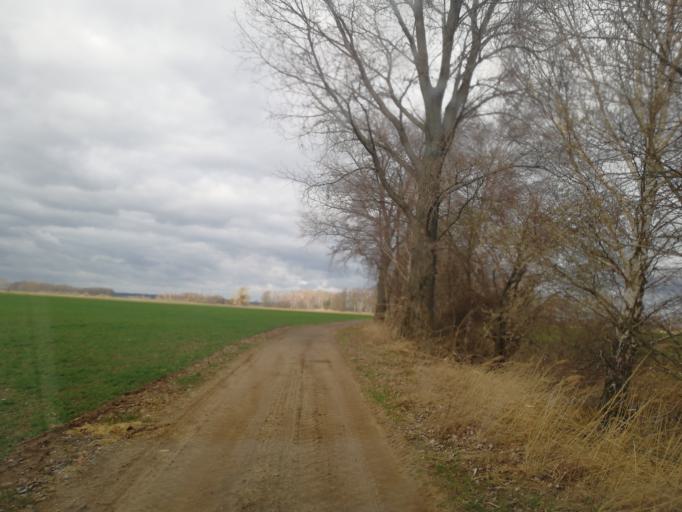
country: DE
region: Brandenburg
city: Schonewalde
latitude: 51.6684
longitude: 13.5620
